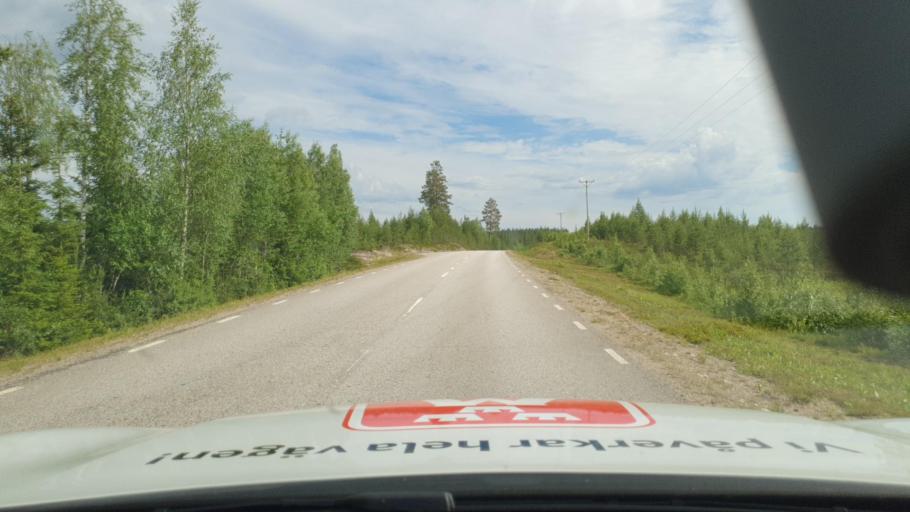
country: NO
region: Hedmark
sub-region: Trysil
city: Innbygda
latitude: 60.9927
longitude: 12.4920
